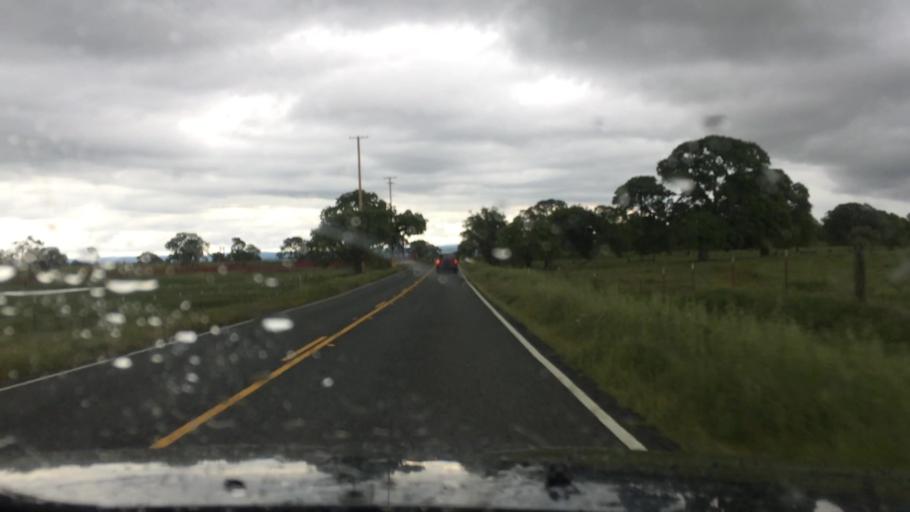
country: US
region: California
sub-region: Amador County
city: Ione
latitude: 38.3867
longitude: -121.0447
